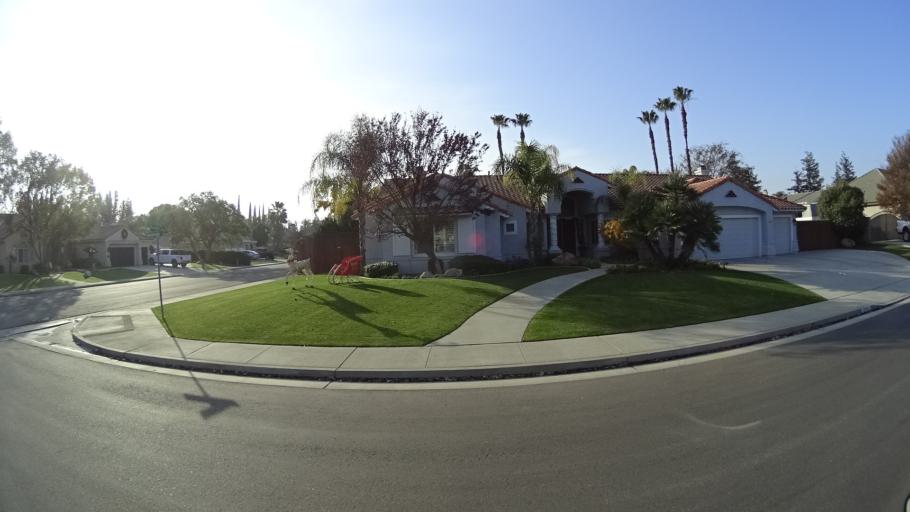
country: US
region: California
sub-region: Kern County
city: Rosedale
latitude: 35.3721
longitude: -119.1438
